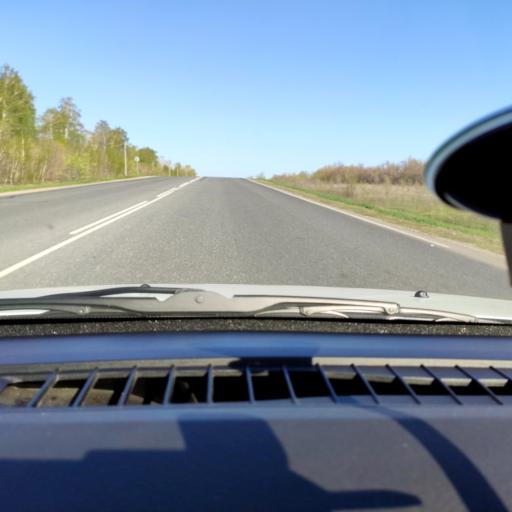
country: RU
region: Samara
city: Dubovyy Umet
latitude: 53.0757
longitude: 50.3551
